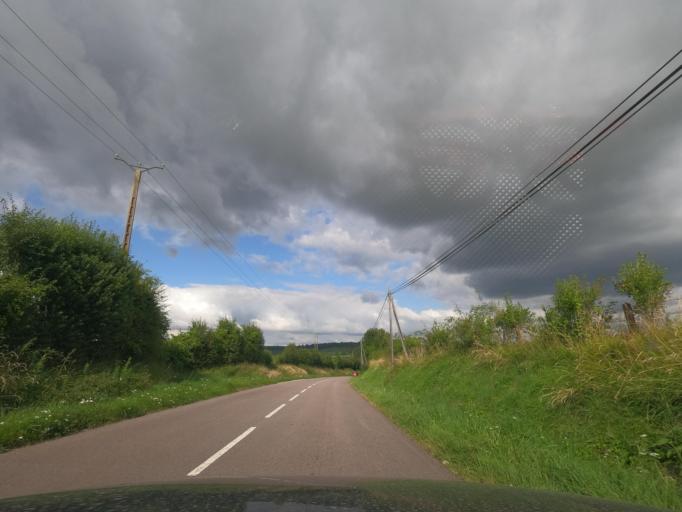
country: FR
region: Lower Normandy
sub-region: Departement de l'Orne
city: Gace
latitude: 48.7933
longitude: 0.2828
